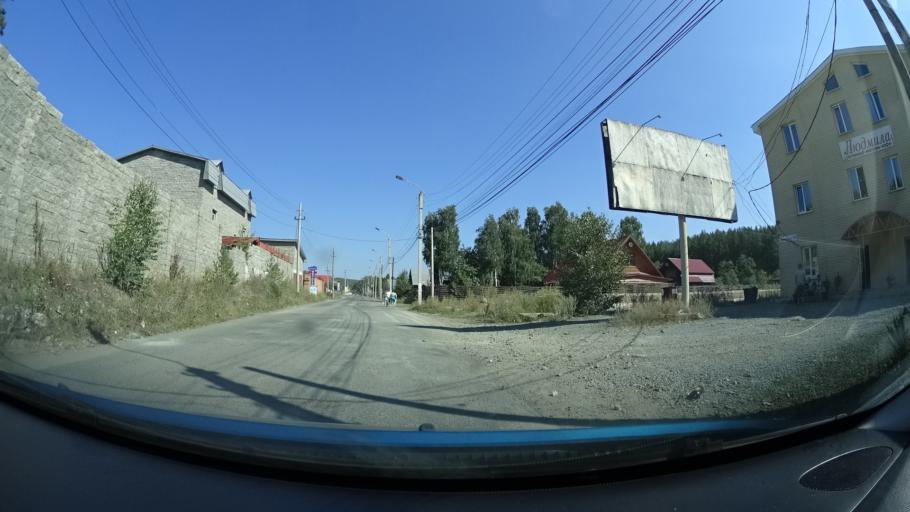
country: RU
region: Bashkortostan
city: Abzakovo
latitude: 53.8069
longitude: 58.6361
